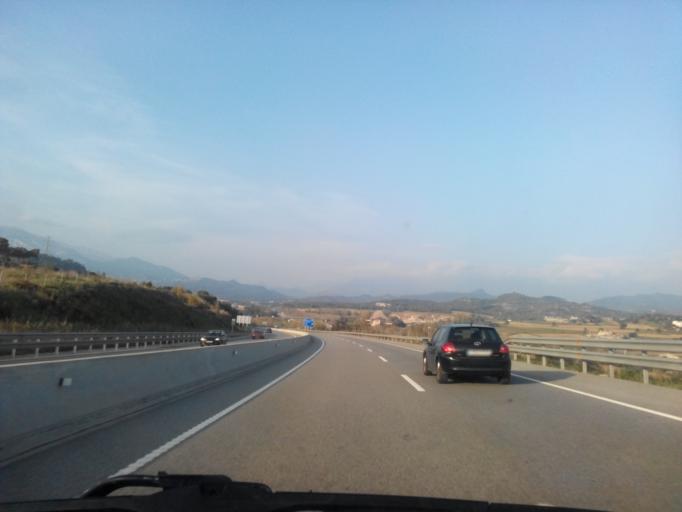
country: ES
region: Catalonia
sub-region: Provincia de Barcelona
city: Gironella
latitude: 42.0368
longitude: 1.8752
